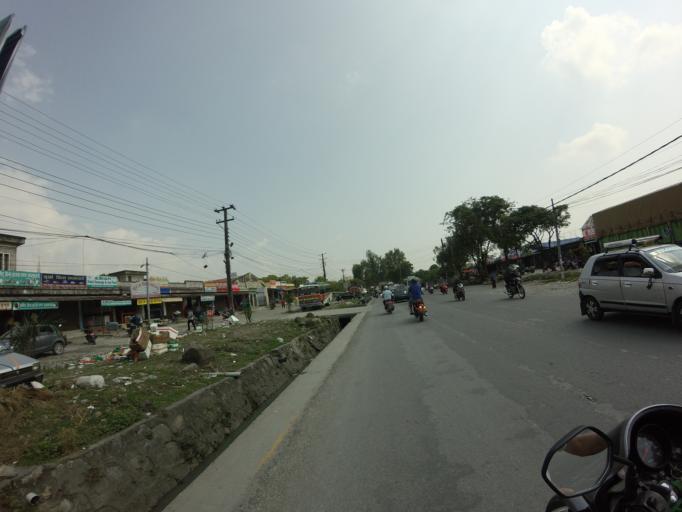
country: NP
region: Western Region
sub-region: Gandaki Zone
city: Pokhara
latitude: 28.2084
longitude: 83.9884
